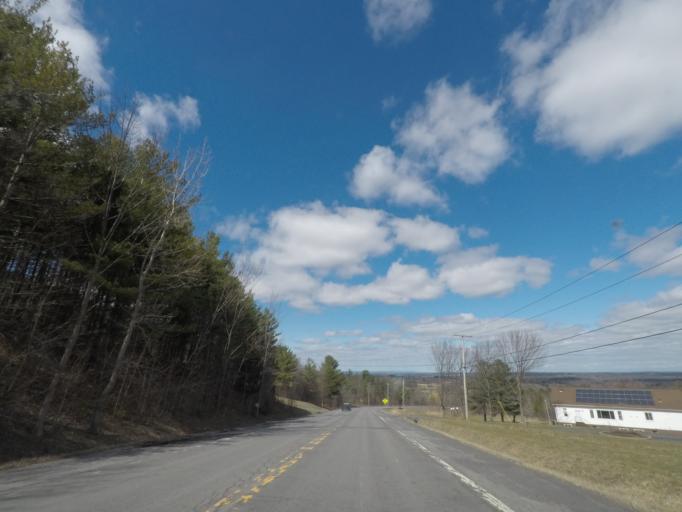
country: US
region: New York
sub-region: Albany County
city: Voorheesville
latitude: 42.6214
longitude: -73.9754
